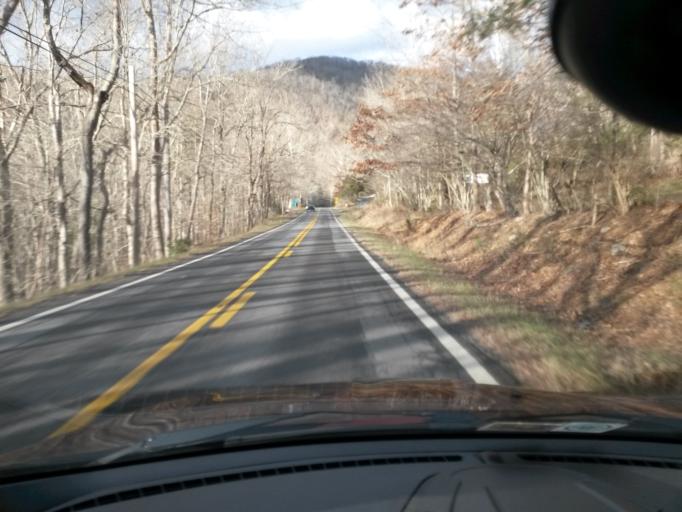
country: US
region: West Virginia
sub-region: Monroe County
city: Union
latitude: 37.5217
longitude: -80.6170
